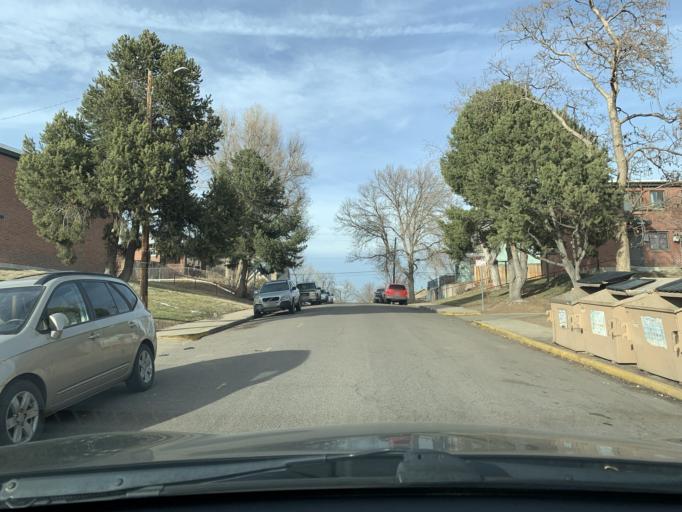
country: US
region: Colorado
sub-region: Jefferson County
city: Edgewater
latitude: 39.7375
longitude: -105.0334
